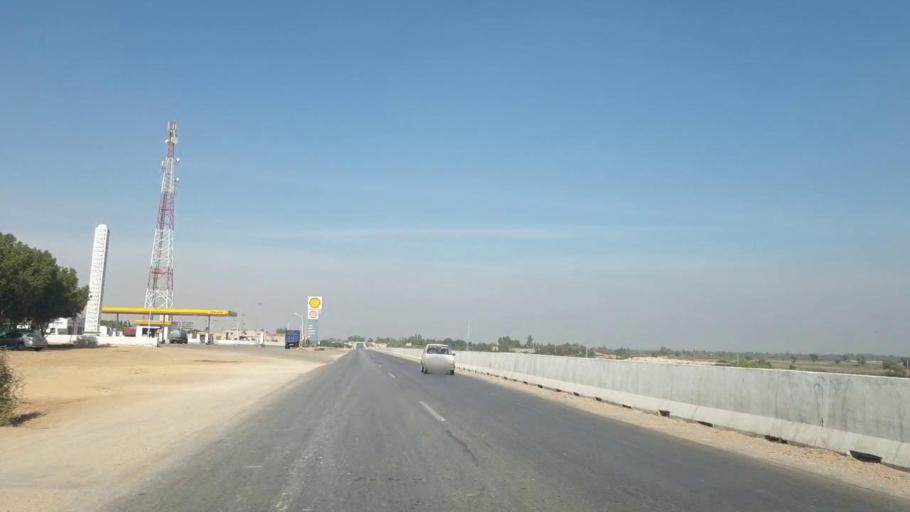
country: PK
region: Sindh
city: Hala
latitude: 25.7040
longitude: 68.2957
